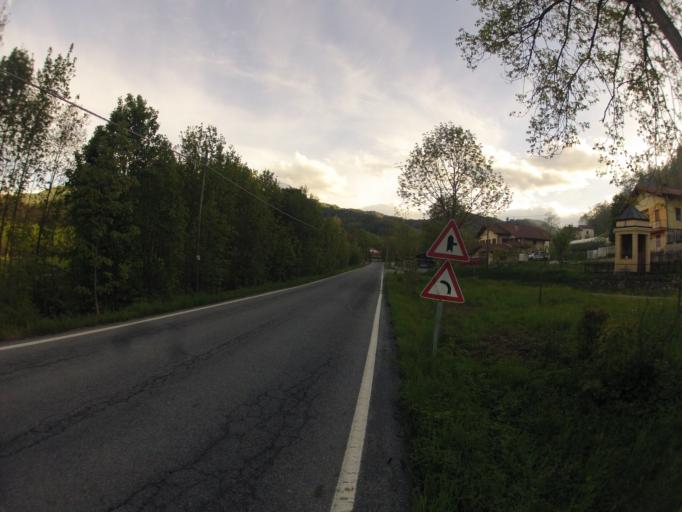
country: IT
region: Piedmont
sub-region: Provincia di Cuneo
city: Peveragno
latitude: 44.3220
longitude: 7.5995
